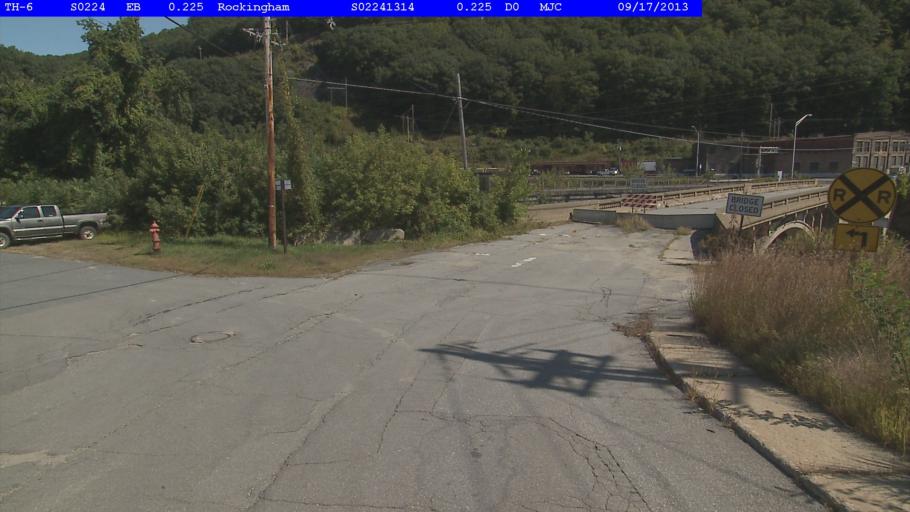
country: US
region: Vermont
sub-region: Windham County
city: Bellows Falls
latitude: 43.1353
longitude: -72.4411
